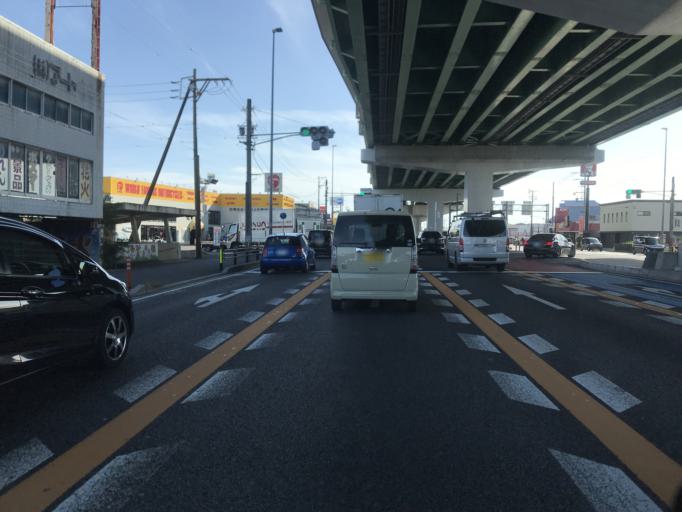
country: JP
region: Aichi
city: Iwakura
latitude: 35.2472
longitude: 136.8450
